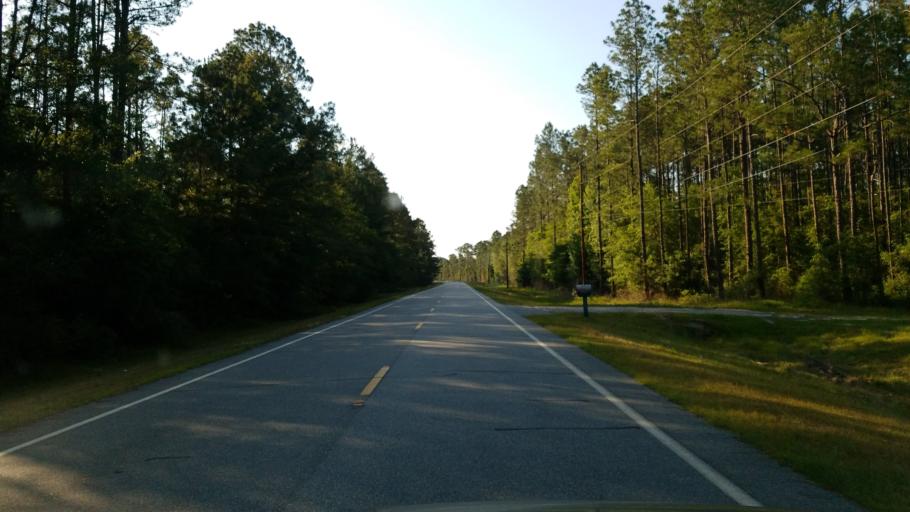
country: US
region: Georgia
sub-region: Lanier County
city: Lakeland
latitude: 30.8924
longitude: -83.0566
